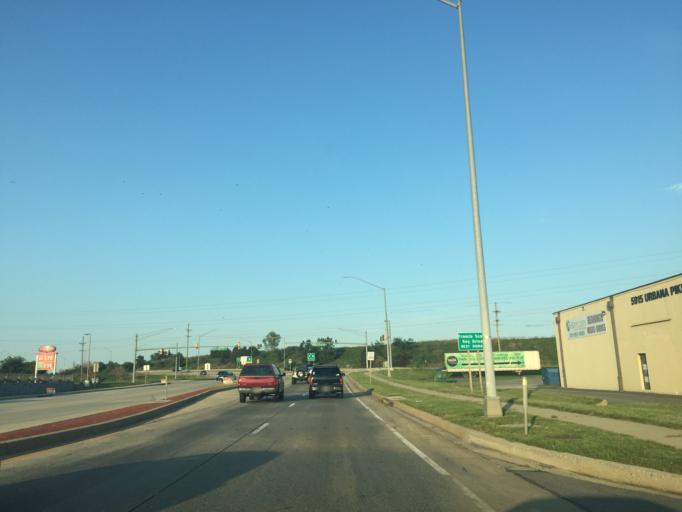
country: US
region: Maryland
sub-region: Frederick County
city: Frederick
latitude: 39.3983
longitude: -77.4065
